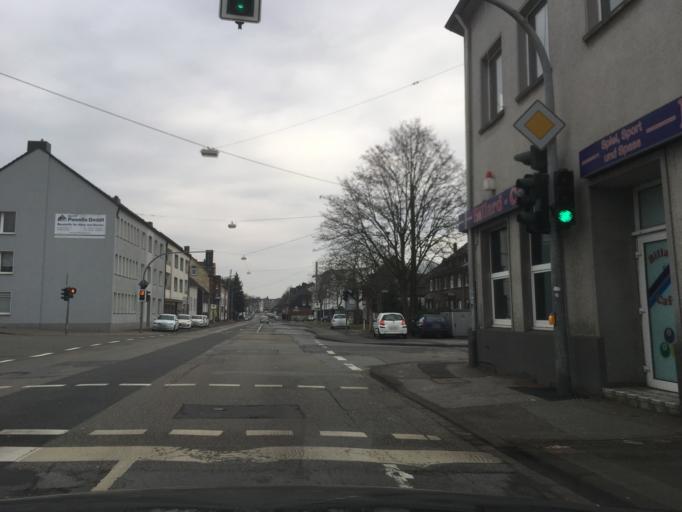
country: DE
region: North Rhine-Westphalia
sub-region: Regierungsbezirk Munster
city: Bottrop
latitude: 51.5294
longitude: 6.9409
